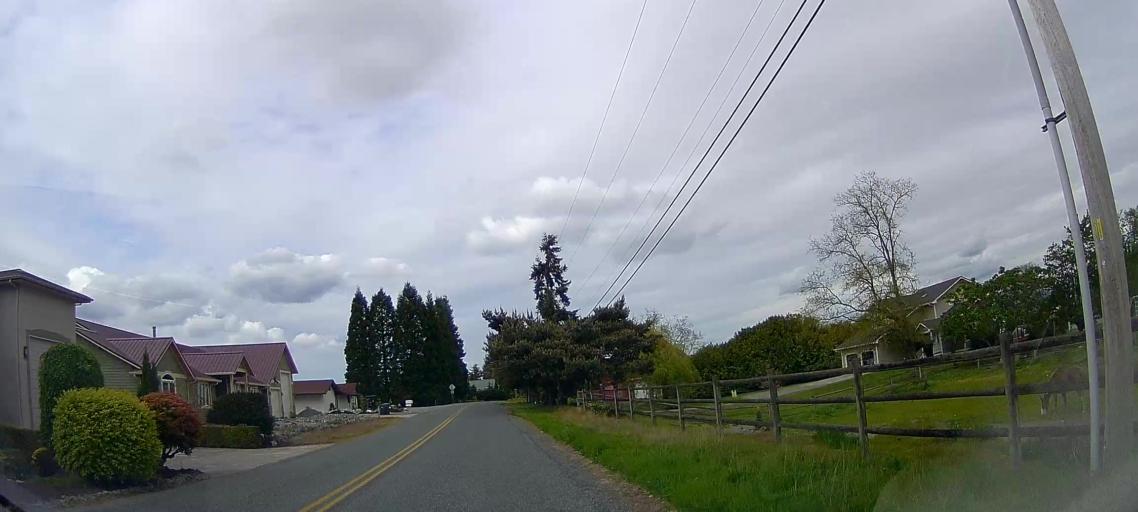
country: US
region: Washington
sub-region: Skagit County
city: Anacortes
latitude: 48.4217
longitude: -122.4995
